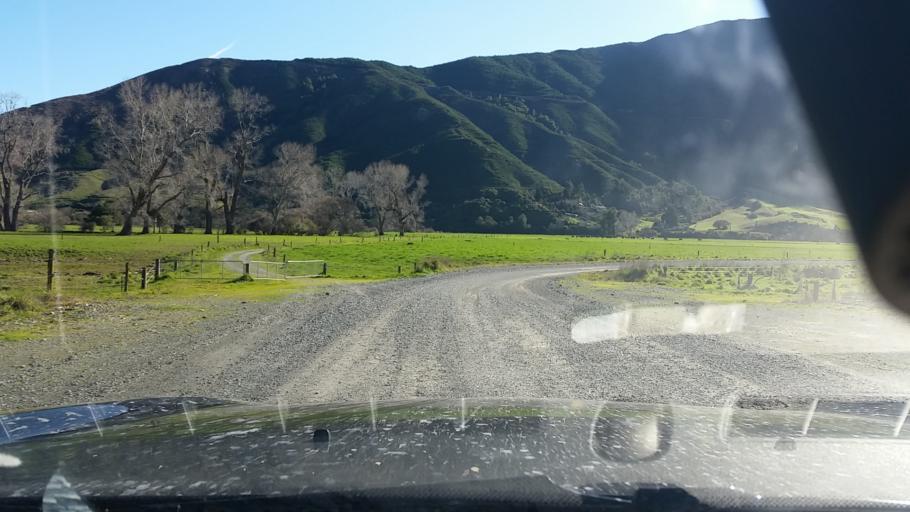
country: NZ
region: Marlborough
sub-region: Marlborough District
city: Picton
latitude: -41.2738
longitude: 173.7303
